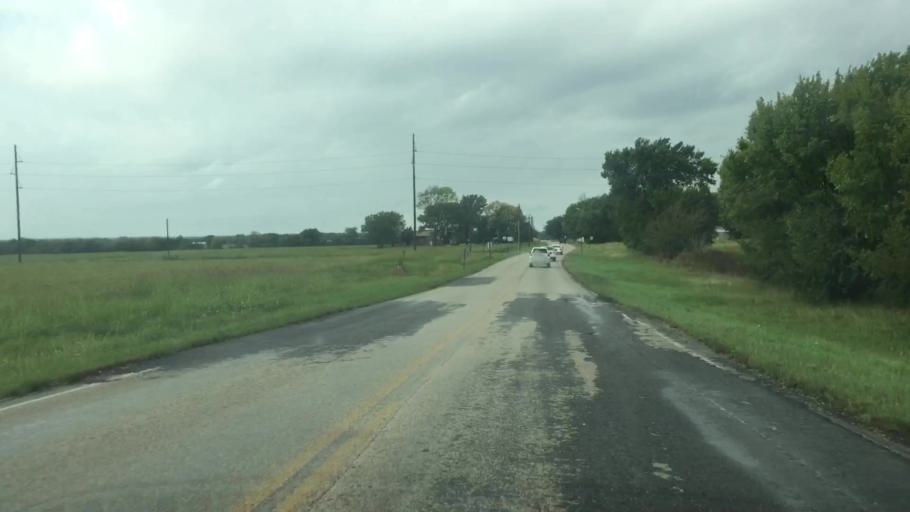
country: US
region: Kansas
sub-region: Allen County
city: Iola
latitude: 37.8857
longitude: -95.4167
